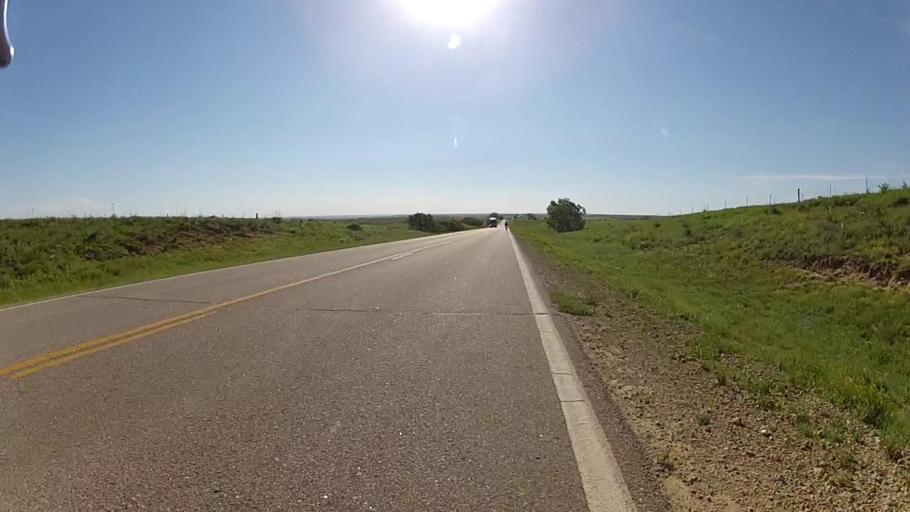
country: US
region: Kansas
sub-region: Barber County
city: Medicine Lodge
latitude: 37.2816
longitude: -98.8960
